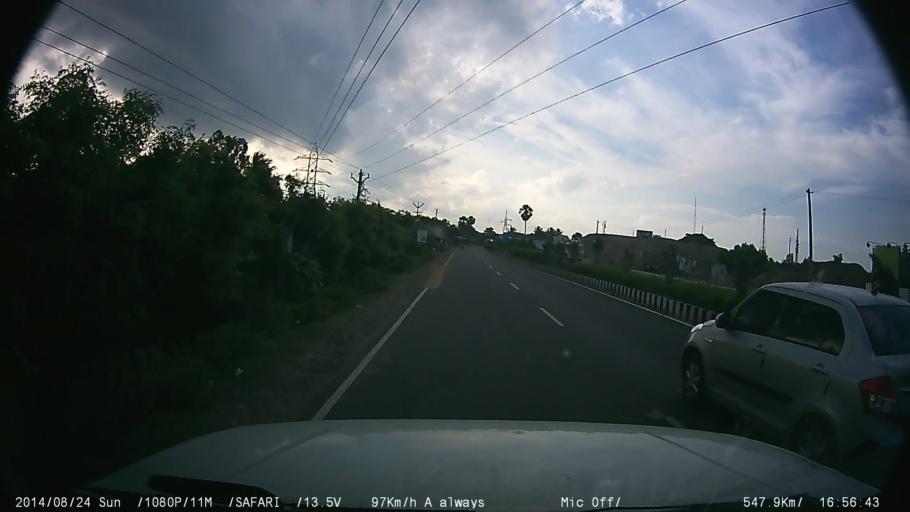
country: IN
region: Tamil Nadu
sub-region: Kancheepuram
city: Vengavasal
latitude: 12.8346
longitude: 80.1572
